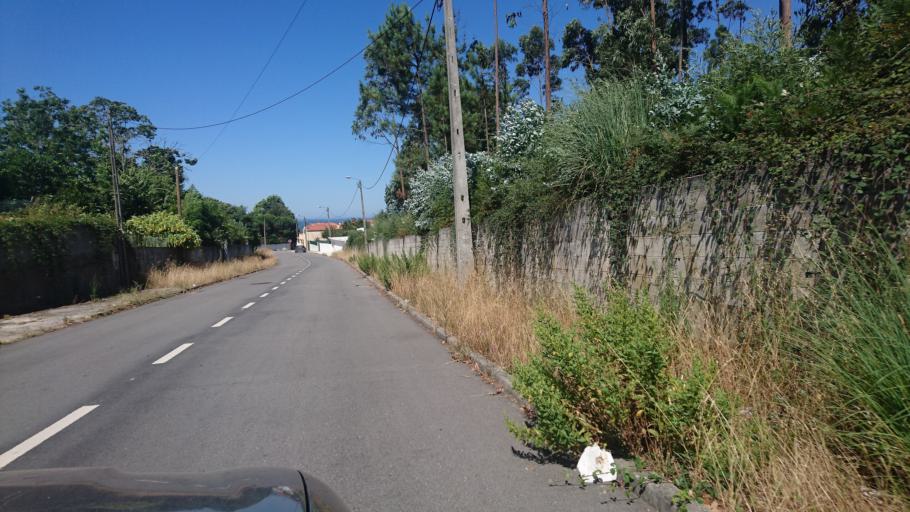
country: PT
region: Aveiro
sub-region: Ovar
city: Esmoriz
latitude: 40.9620
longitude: -8.6141
